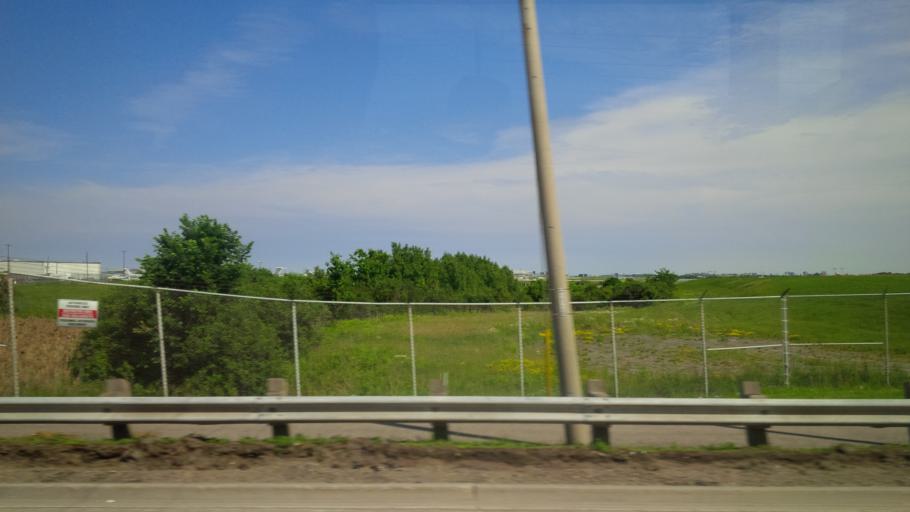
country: CA
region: Ontario
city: Etobicoke
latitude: 43.6905
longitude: -79.6569
